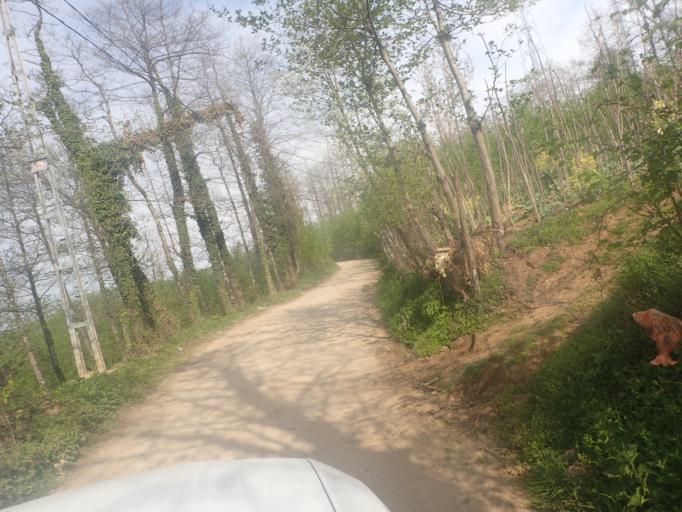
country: TR
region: Ordu
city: Catalpinar
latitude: 40.8819
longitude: 37.4877
